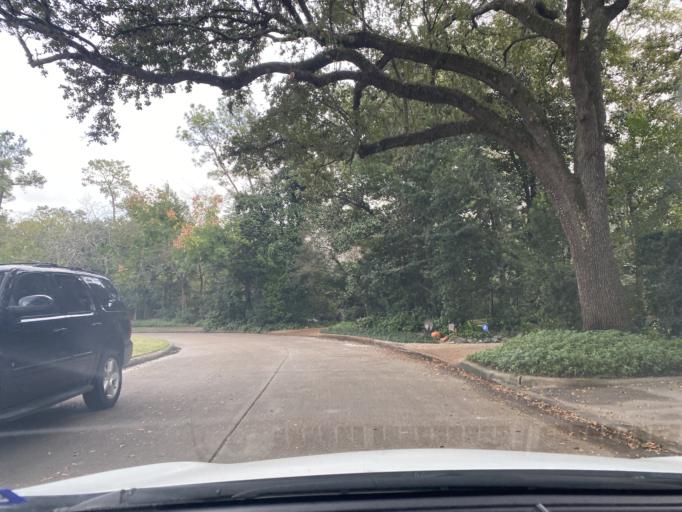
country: US
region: Texas
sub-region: Harris County
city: Hunters Creek Village
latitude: 29.7654
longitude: -95.4674
